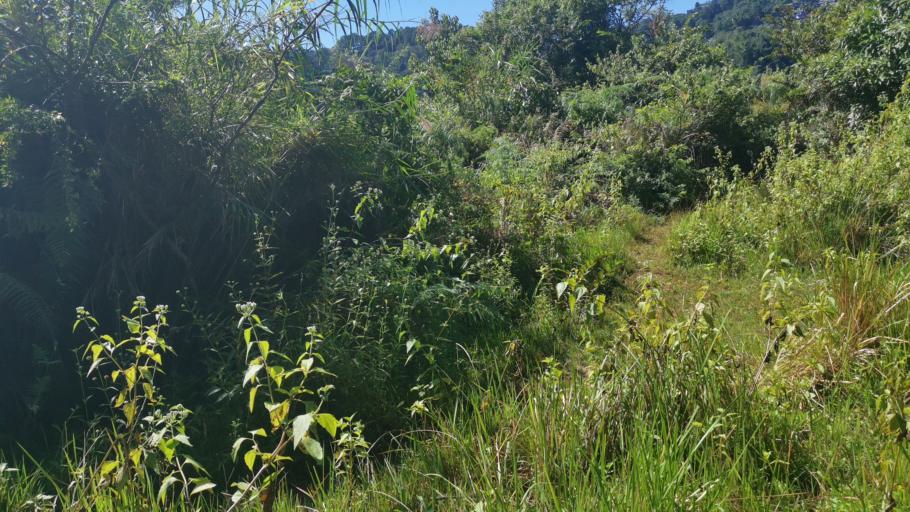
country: PH
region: Cordillera
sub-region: Province of Benguet
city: Tuding
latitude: 16.3863
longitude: 120.6325
